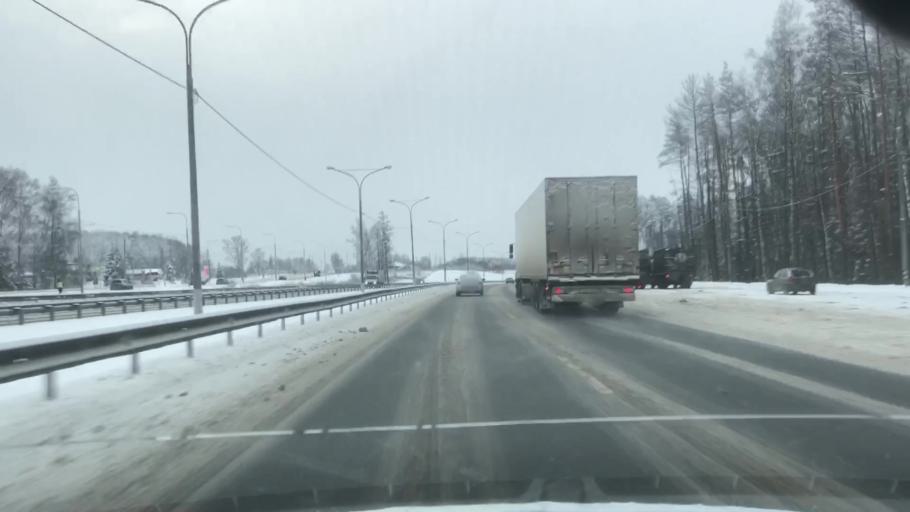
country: RU
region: Moskovskaya
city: Mikhnevo
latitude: 55.1308
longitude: 37.9348
